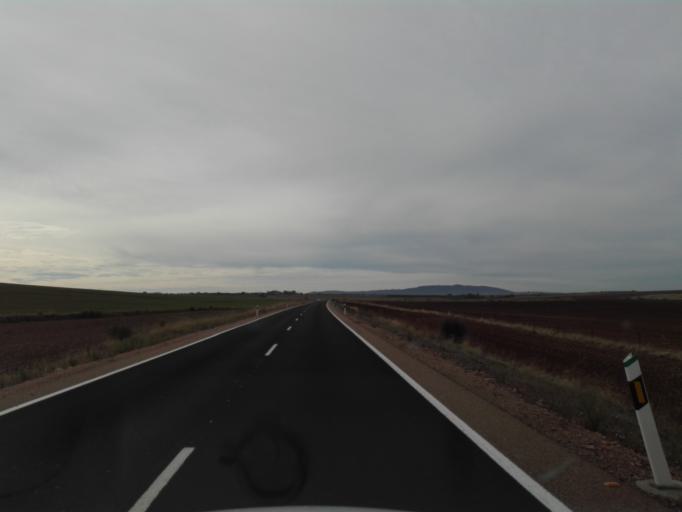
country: ES
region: Extremadura
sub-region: Provincia de Badajoz
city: Valencia de las Torres
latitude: 38.3361
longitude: -5.9642
